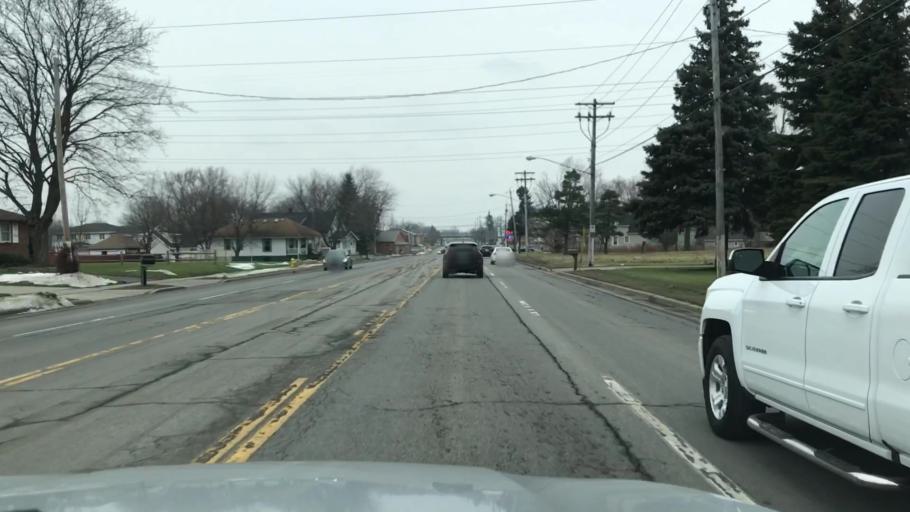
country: US
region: New York
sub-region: Erie County
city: Blasdell
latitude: 42.8064
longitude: -78.7979
